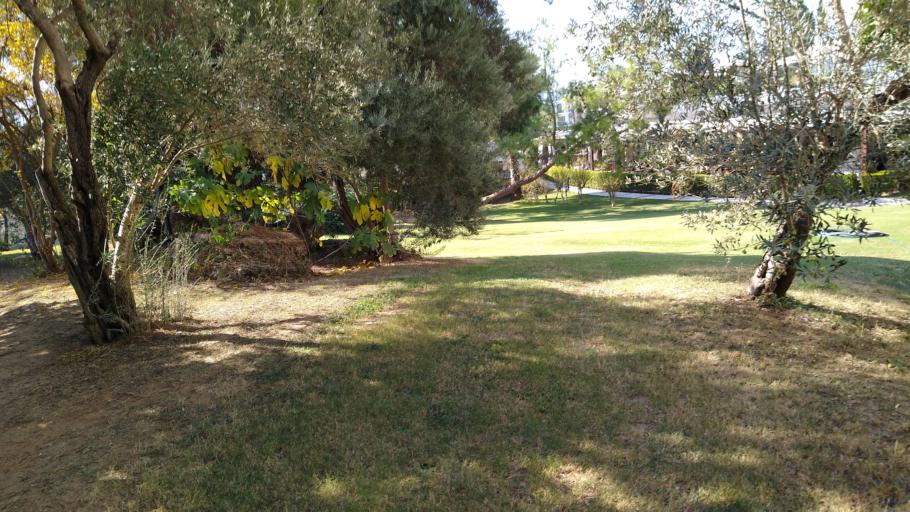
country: TR
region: Antalya
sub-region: Manavgat
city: Manavgat
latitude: 36.7512
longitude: 31.4546
